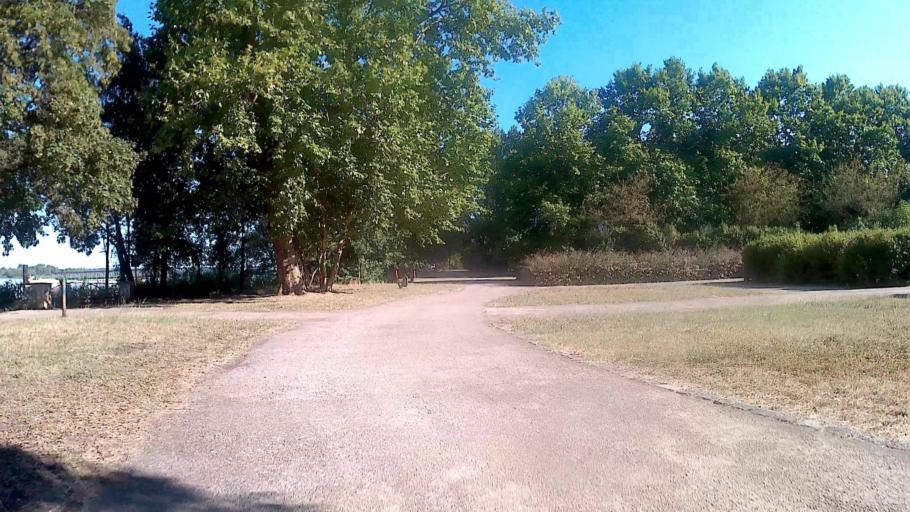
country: FR
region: Aquitaine
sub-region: Departement de la Gironde
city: Begles
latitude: 44.7944
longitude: -0.5277
